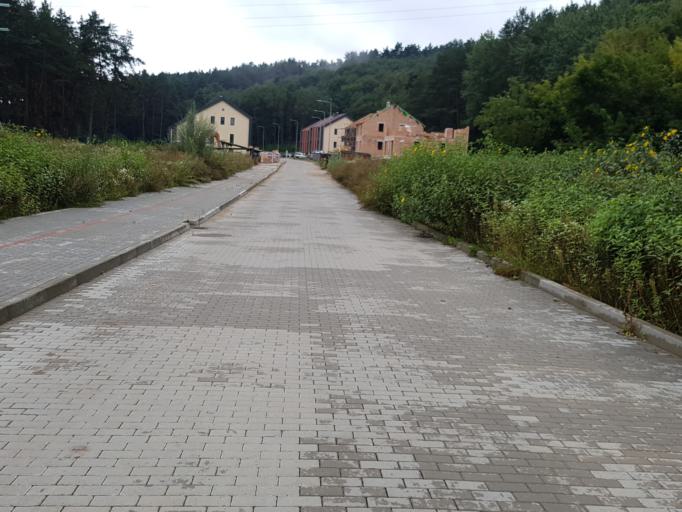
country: LT
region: Vilnius County
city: Lazdynai
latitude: 54.6662
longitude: 25.2234
